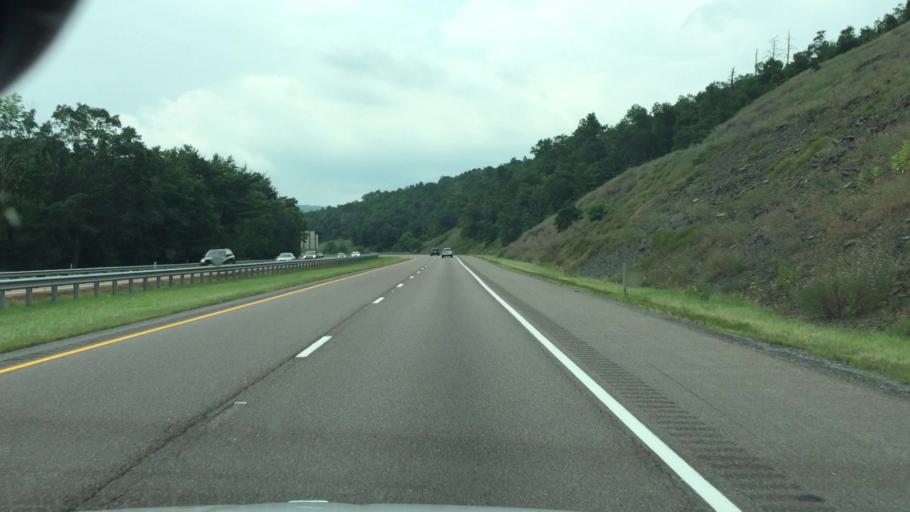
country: US
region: West Virginia
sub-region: Morgan County
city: Berkeley Springs
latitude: 39.6802
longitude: -78.4797
